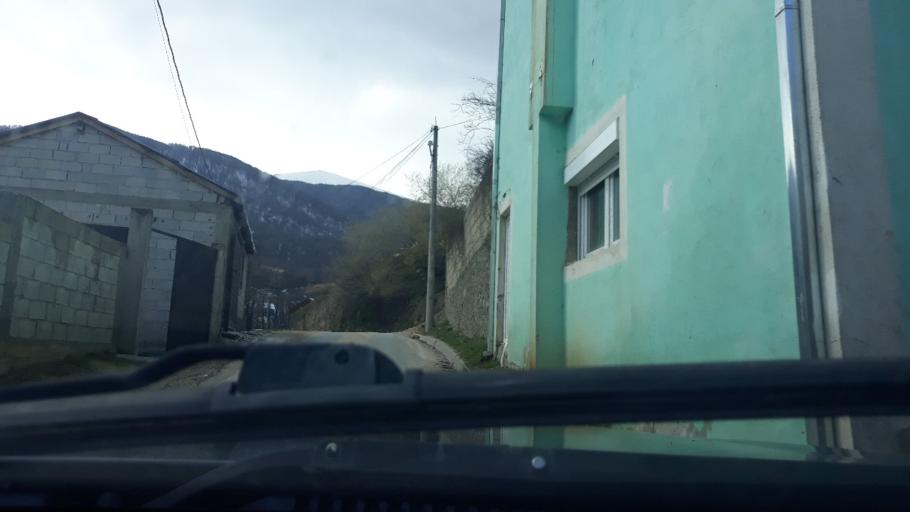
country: MK
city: Bogomila
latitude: 41.7278
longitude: 21.4894
